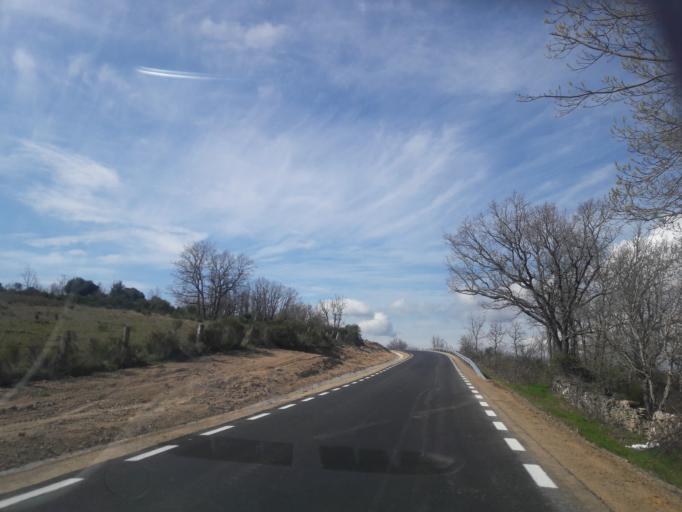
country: ES
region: Castille and Leon
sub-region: Provincia de Salamanca
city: Monleon
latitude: 40.5279
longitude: -5.8358
